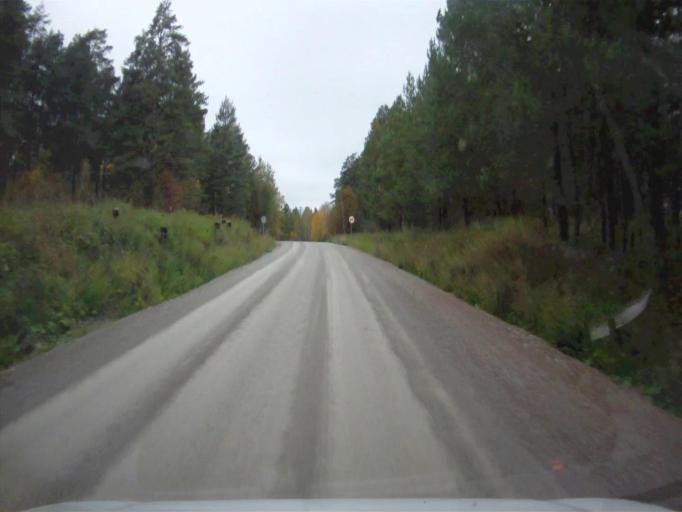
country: RU
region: Chelyabinsk
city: Nyazepetrovsk
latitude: 56.0618
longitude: 59.4483
